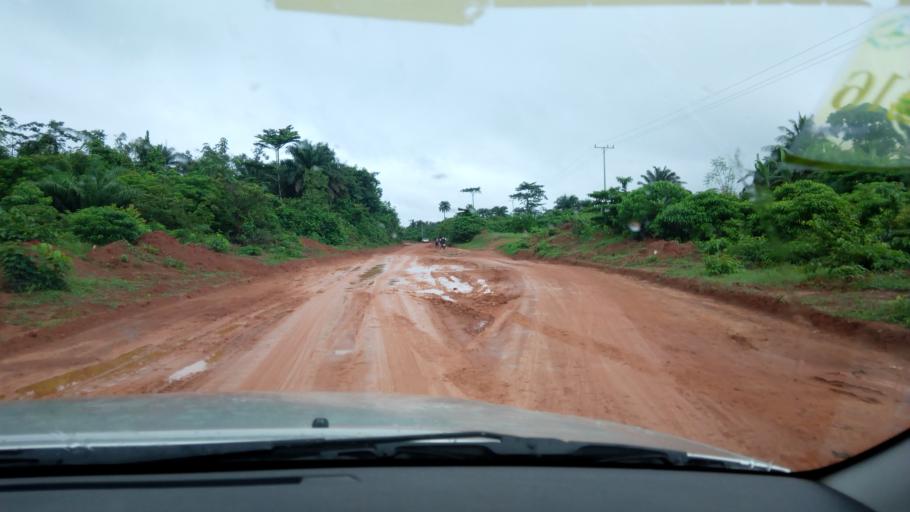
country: LR
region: Nimba
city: Sanniquellie
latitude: 7.1834
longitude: -8.9687
